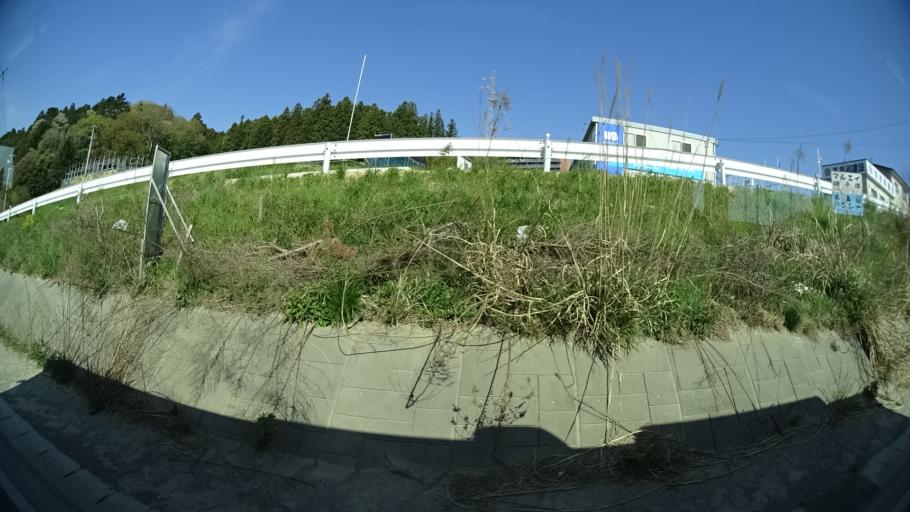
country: JP
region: Iwate
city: Ofunato
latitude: 39.0250
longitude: 141.6250
